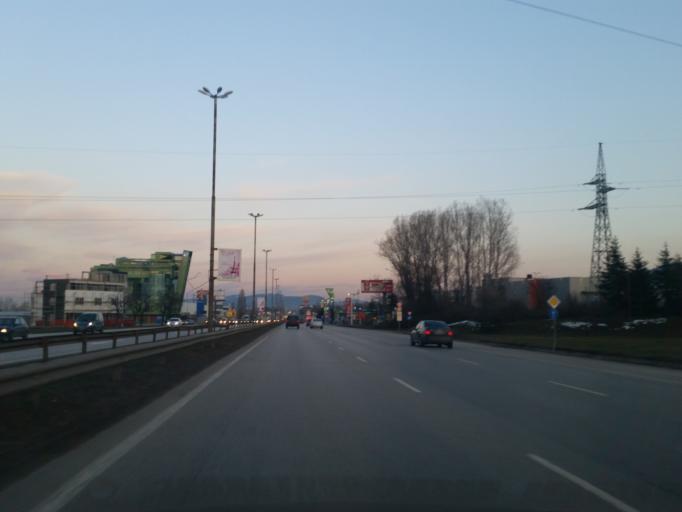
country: BG
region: Sofia-Capital
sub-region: Stolichna Obshtina
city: Sofia
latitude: 42.6530
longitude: 23.2846
